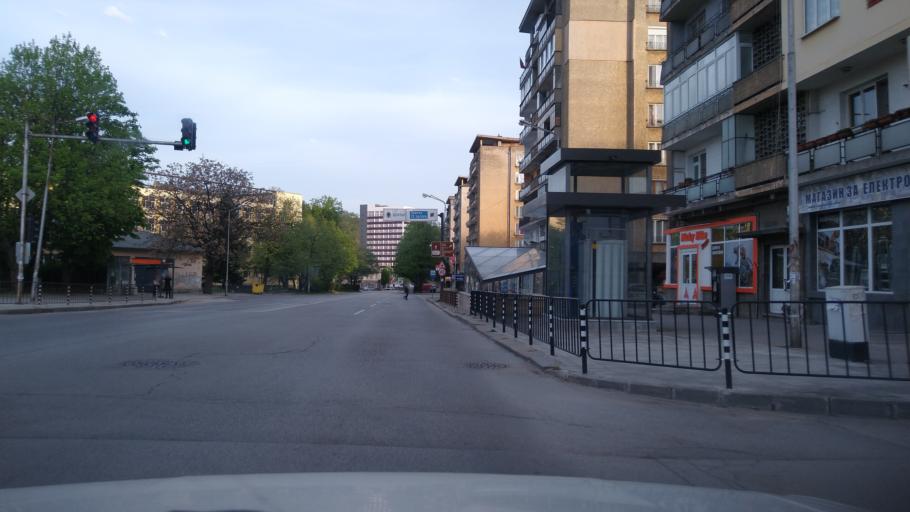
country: BG
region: Gabrovo
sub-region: Obshtina Gabrovo
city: Gabrovo
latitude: 42.8789
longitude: 25.3149
